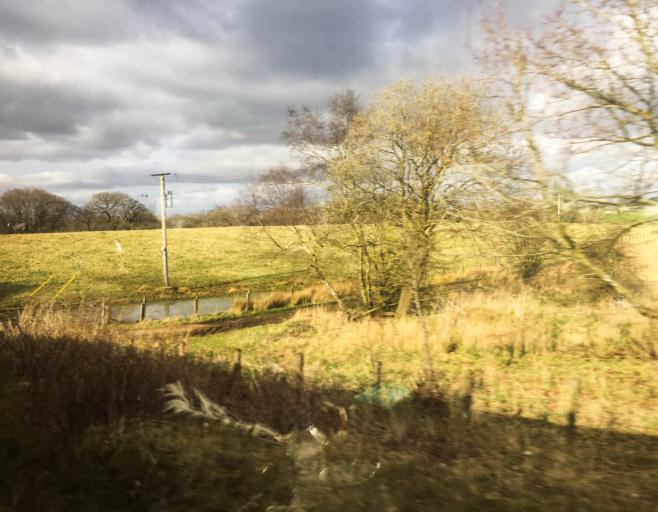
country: GB
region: Scotland
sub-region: South Lanarkshire
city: Carluke
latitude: 55.7093
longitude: -3.8266
